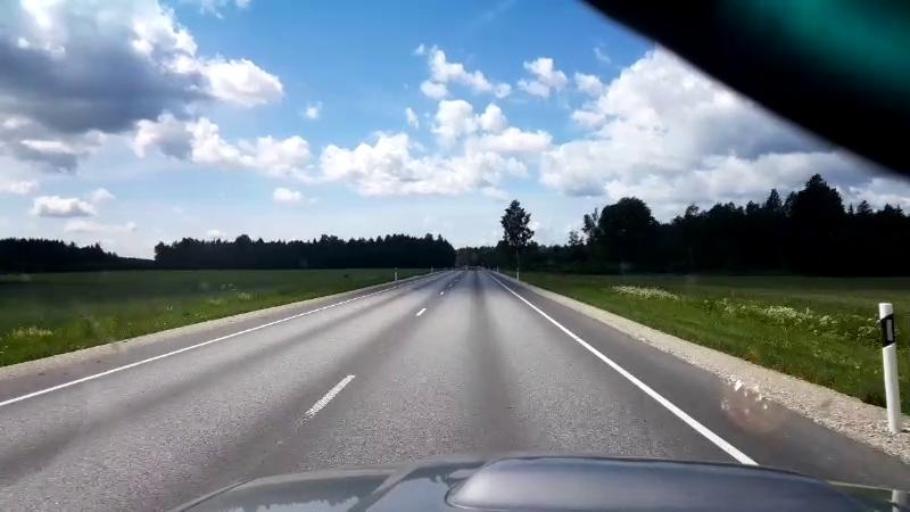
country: EE
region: Jaervamaa
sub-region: Paide linn
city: Paide
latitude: 59.0096
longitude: 25.6910
